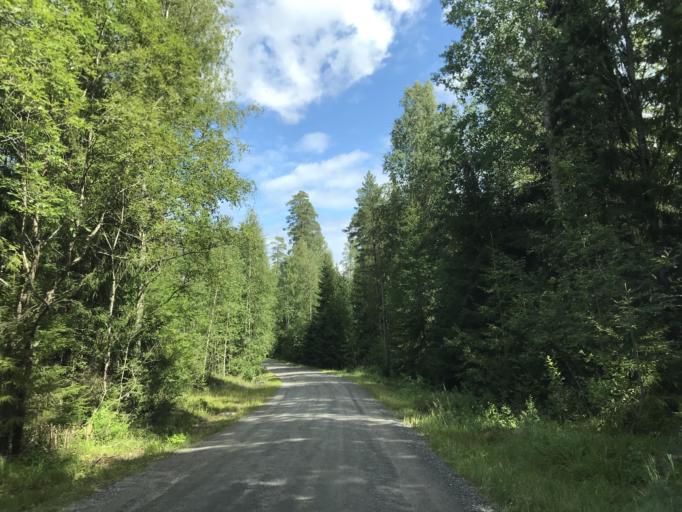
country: FI
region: Uusimaa
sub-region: Helsinki
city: Kaerkoelae
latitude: 60.6341
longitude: 23.7791
